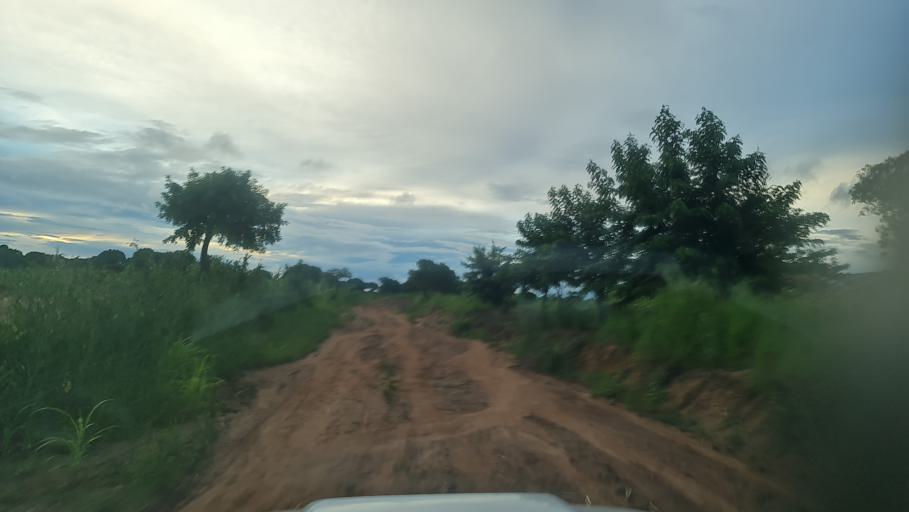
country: MZ
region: Nampula
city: Nacala
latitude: -14.7414
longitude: 39.9457
